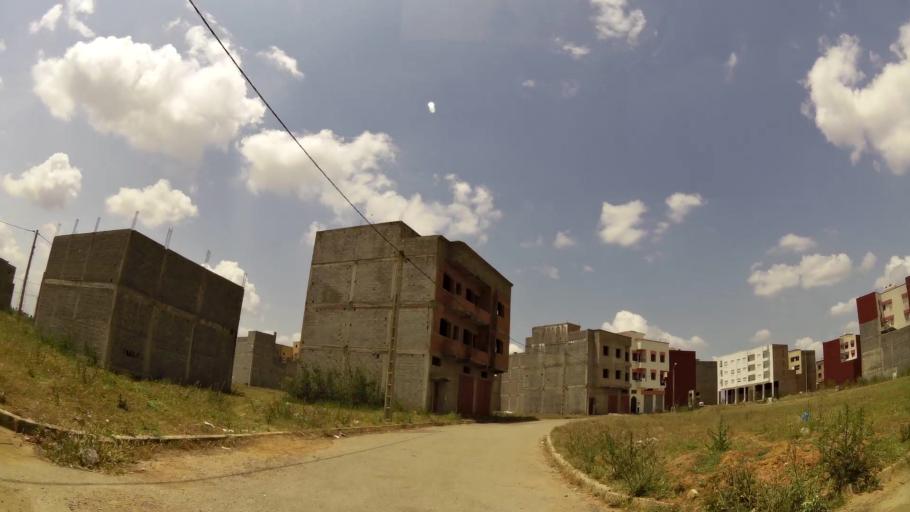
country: MA
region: Rabat-Sale-Zemmour-Zaer
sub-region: Khemisset
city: Tiflet
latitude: 34.0091
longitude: -6.5221
